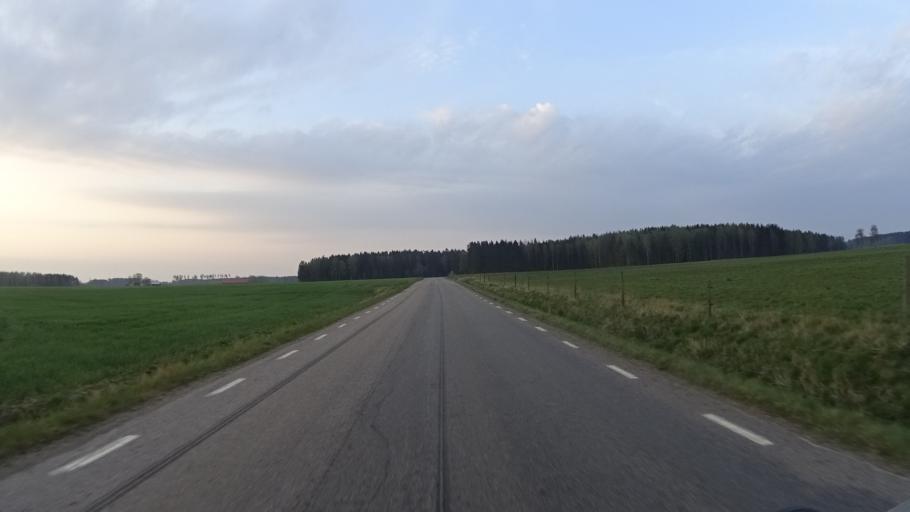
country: SE
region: Vaestra Goetaland
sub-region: Gotene Kommun
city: Kallby
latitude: 58.4621
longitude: 13.3349
